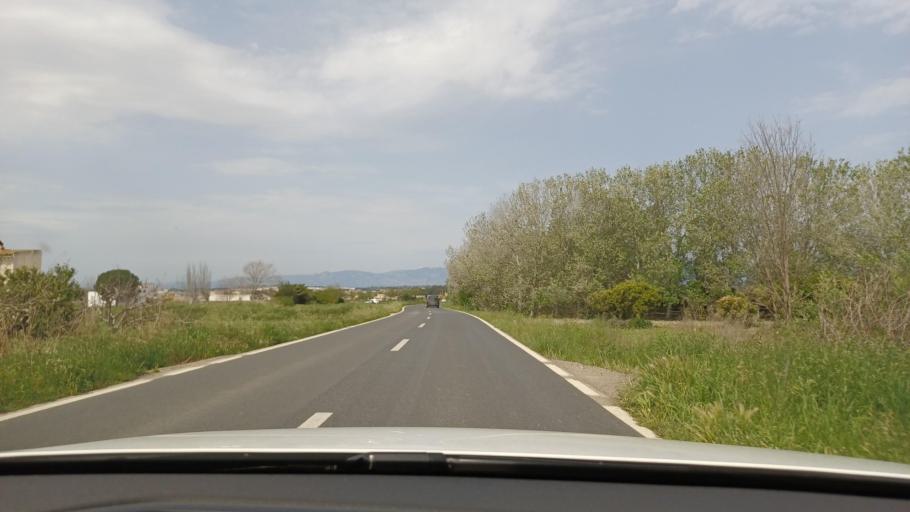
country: ES
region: Catalonia
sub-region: Provincia de Tarragona
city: Amposta
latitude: 40.7047
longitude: 0.6029
